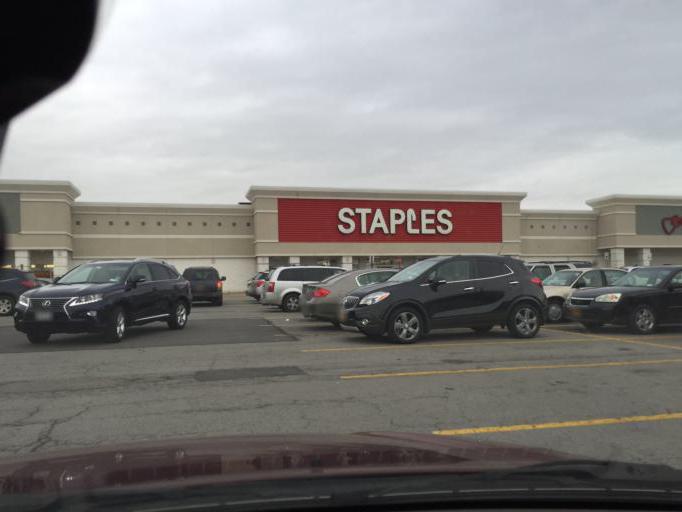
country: US
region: New York
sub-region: Monroe County
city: Rochester
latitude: 43.0884
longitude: -77.6078
